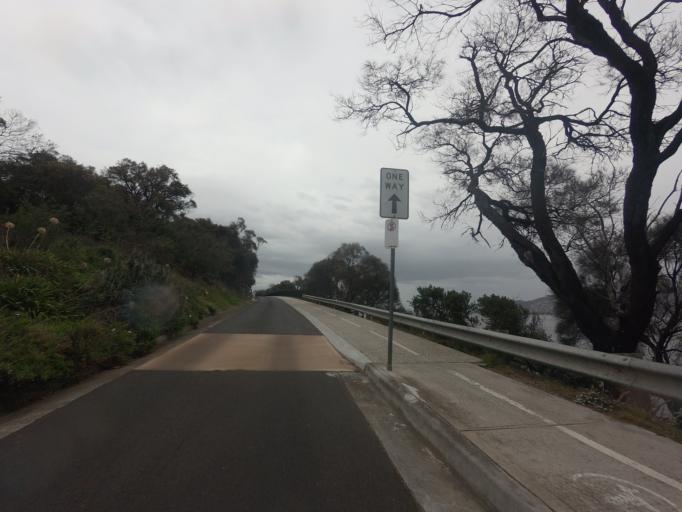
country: AU
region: Tasmania
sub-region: Clarence
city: Bellerive
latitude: -42.8813
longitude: 147.3655
